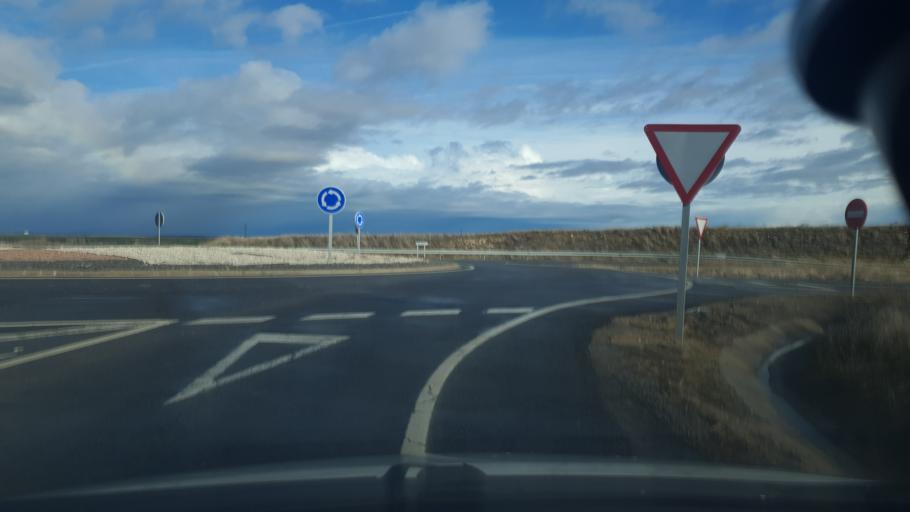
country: ES
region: Castille and Leon
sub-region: Provincia de Segovia
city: Carbonero el Mayor
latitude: 41.1411
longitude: -4.2675
